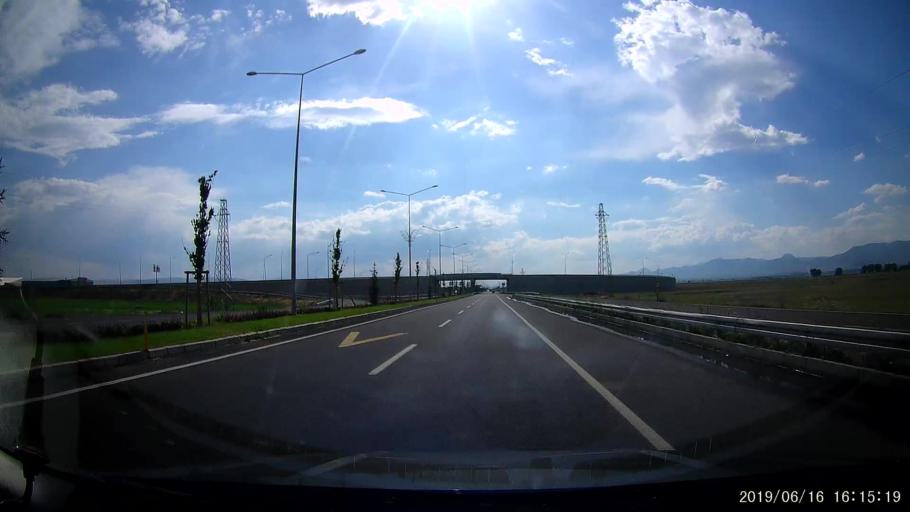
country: TR
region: Erzurum
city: Erzurum
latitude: 39.9618
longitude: 41.2287
